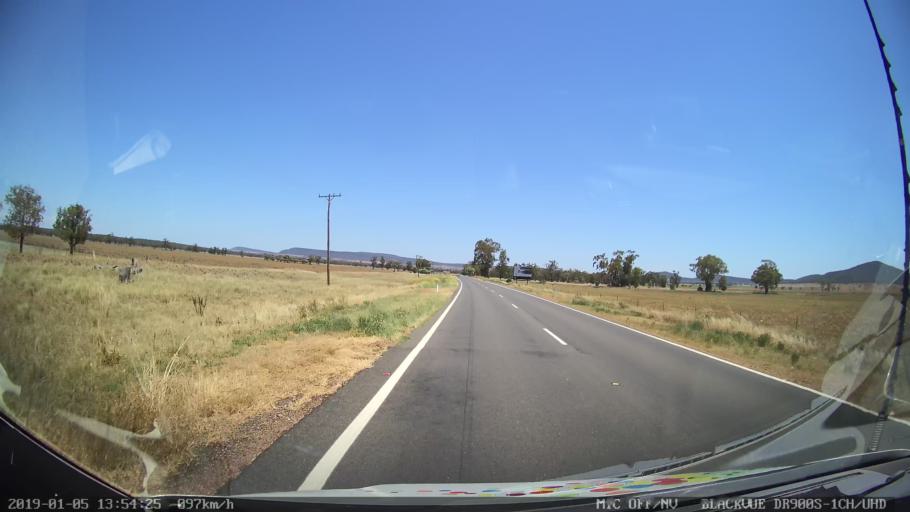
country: AU
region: New South Wales
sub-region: Gunnedah
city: Gunnedah
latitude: -31.0886
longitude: 150.2740
